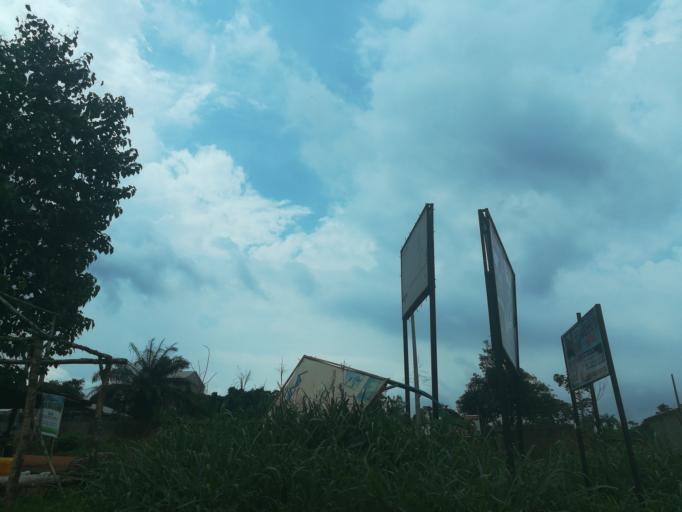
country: NG
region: Lagos
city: Ikorodu
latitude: 6.6736
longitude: 3.6488
